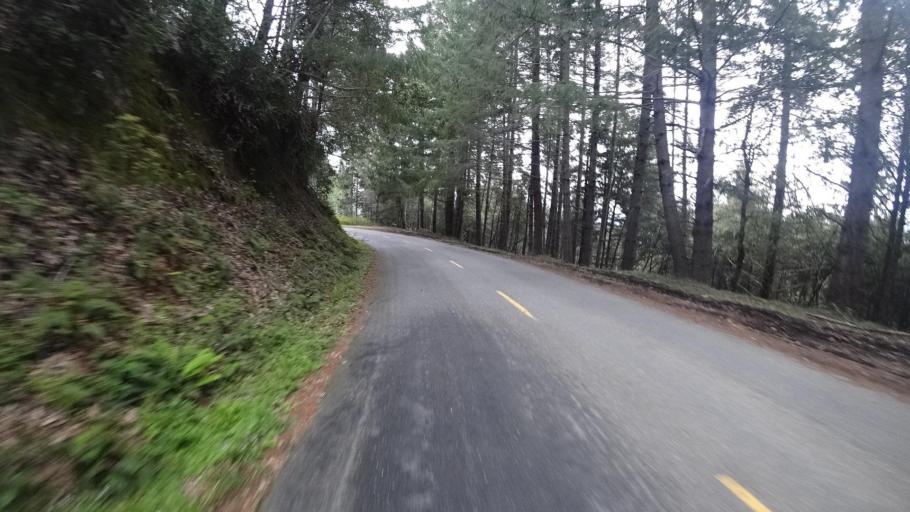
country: US
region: California
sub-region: Humboldt County
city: Redway
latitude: 40.2768
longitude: -123.7865
